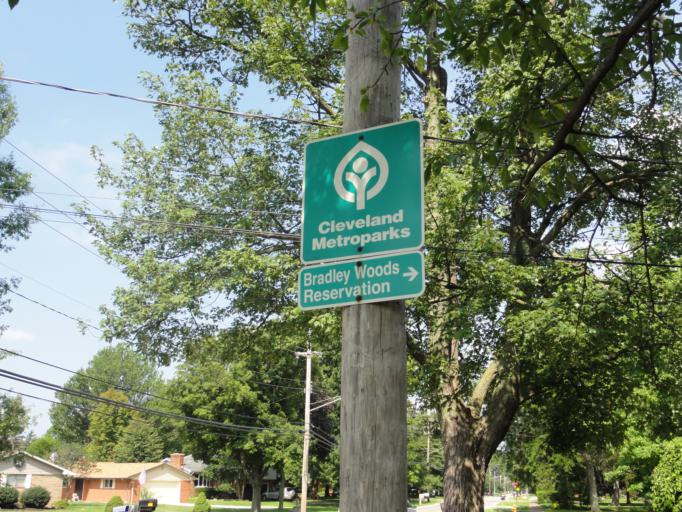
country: US
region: Ohio
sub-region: Cuyahoga County
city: North Olmsted
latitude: 41.4025
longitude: -81.9620
